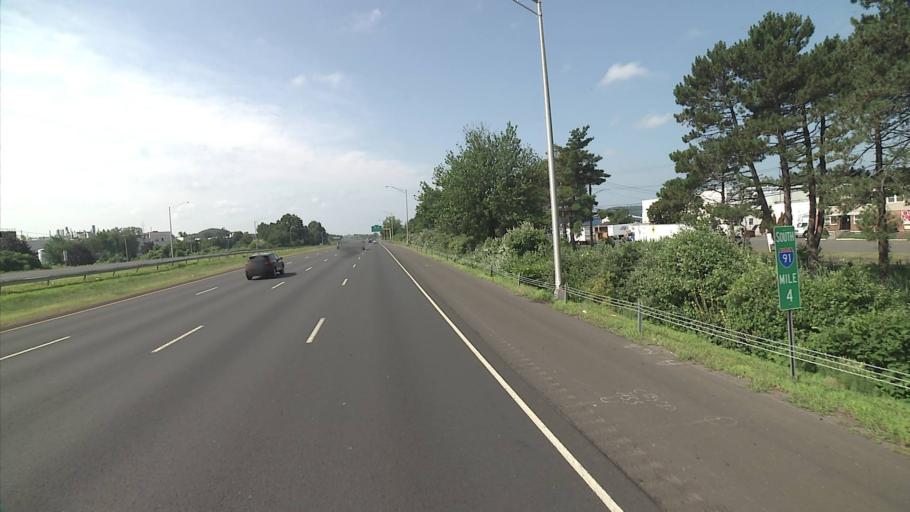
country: US
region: Connecticut
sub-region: New Haven County
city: North Haven
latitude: 41.3414
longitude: -72.8709
